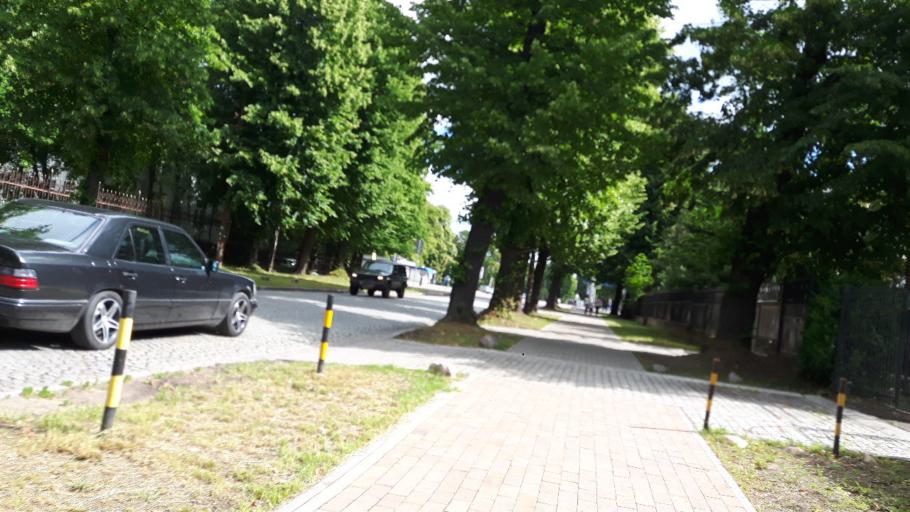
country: RU
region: Kaliningrad
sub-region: Gorod Kaliningrad
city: Kaliningrad
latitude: 54.7356
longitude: 20.5232
